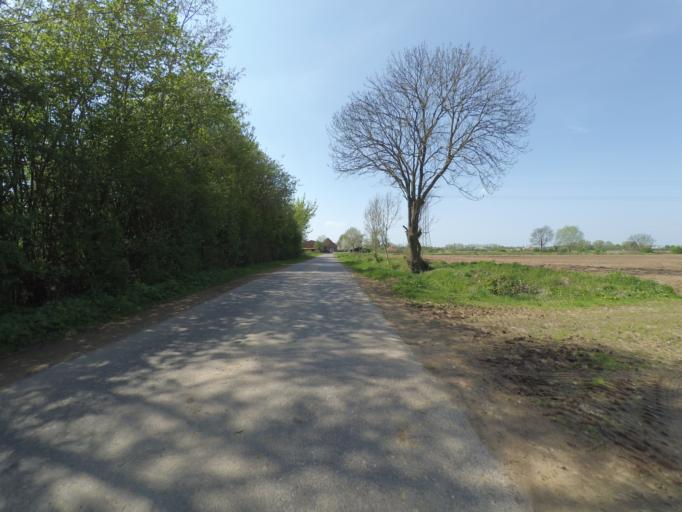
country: DE
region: North Rhine-Westphalia
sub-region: Regierungsbezirk Dusseldorf
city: Emmerich
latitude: 51.8343
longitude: 6.2937
